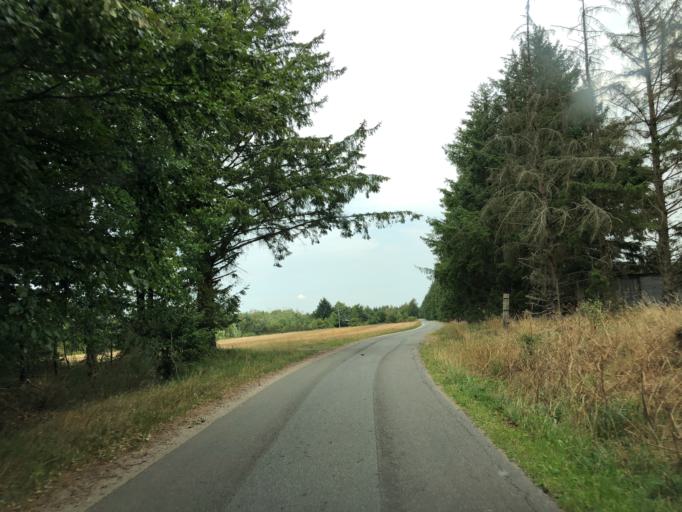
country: DK
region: Central Jutland
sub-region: Holstebro Kommune
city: Ulfborg
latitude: 56.2193
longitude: 8.3210
